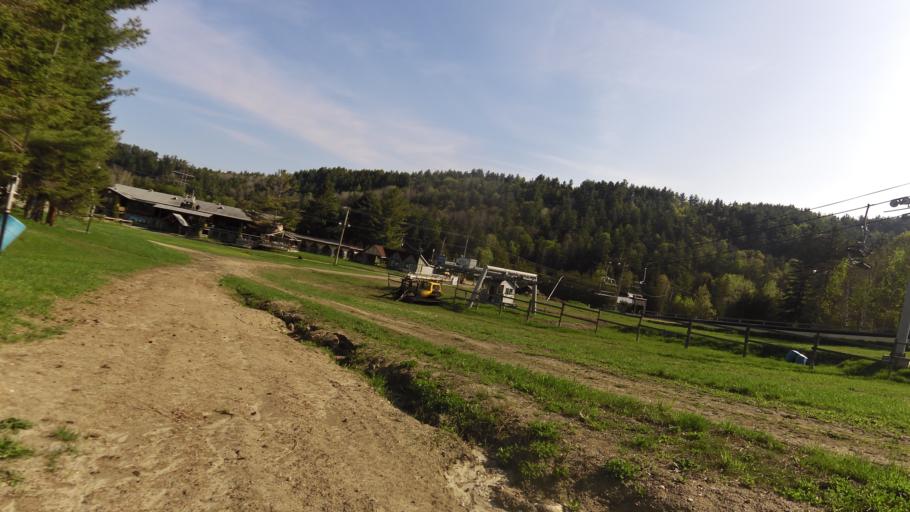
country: CA
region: Quebec
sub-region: Outaouais
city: Wakefield
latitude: 45.6454
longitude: -75.8504
